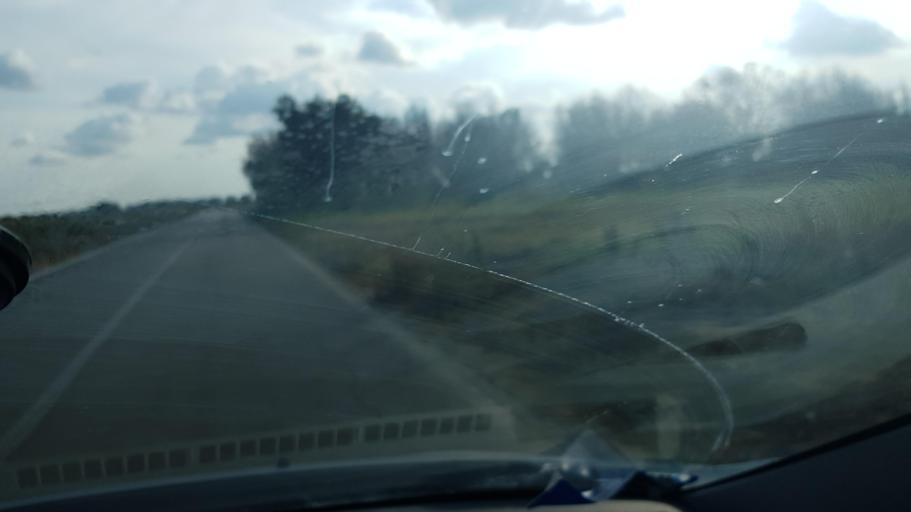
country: IT
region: Apulia
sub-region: Provincia di Brindisi
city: San Donaci
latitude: 40.4340
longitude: 17.9514
